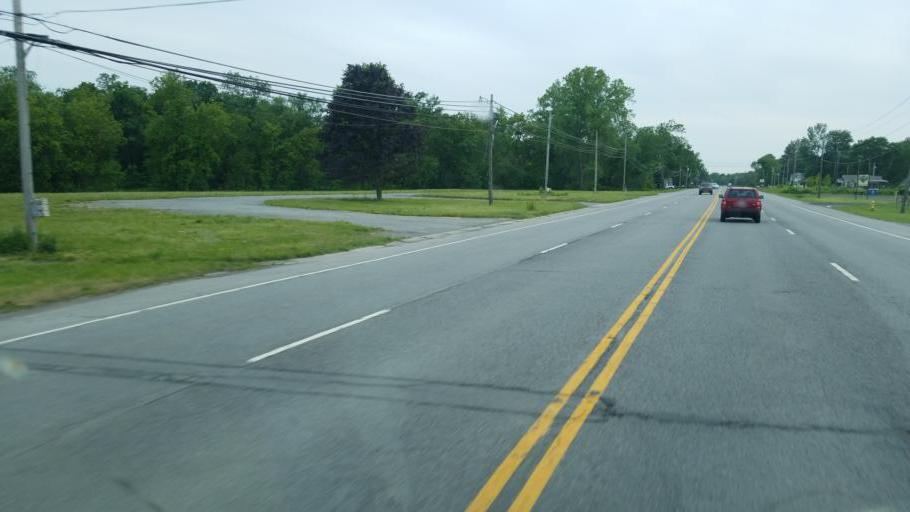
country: US
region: New York
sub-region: Genesee County
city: Batavia
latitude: 43.0075
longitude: -78.2313
